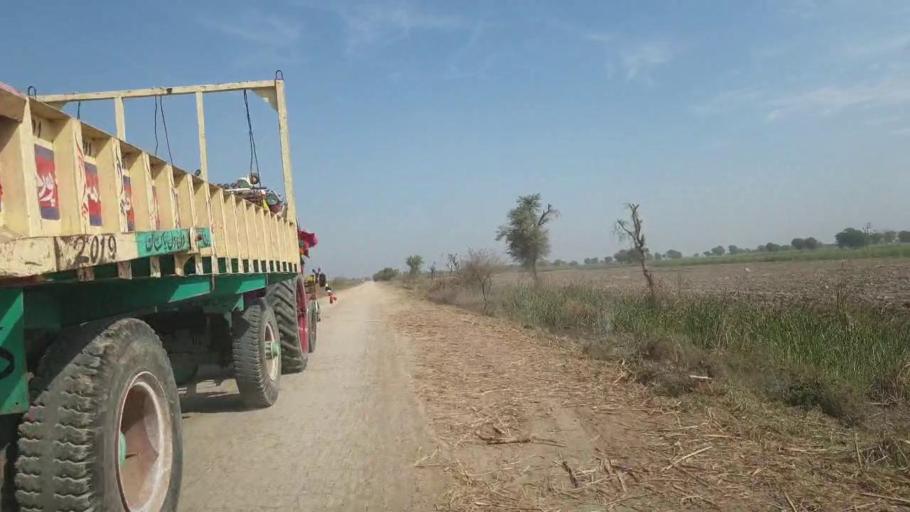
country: PK
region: Sindh
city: Samaro
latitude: 25.3272
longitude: 69.2427
